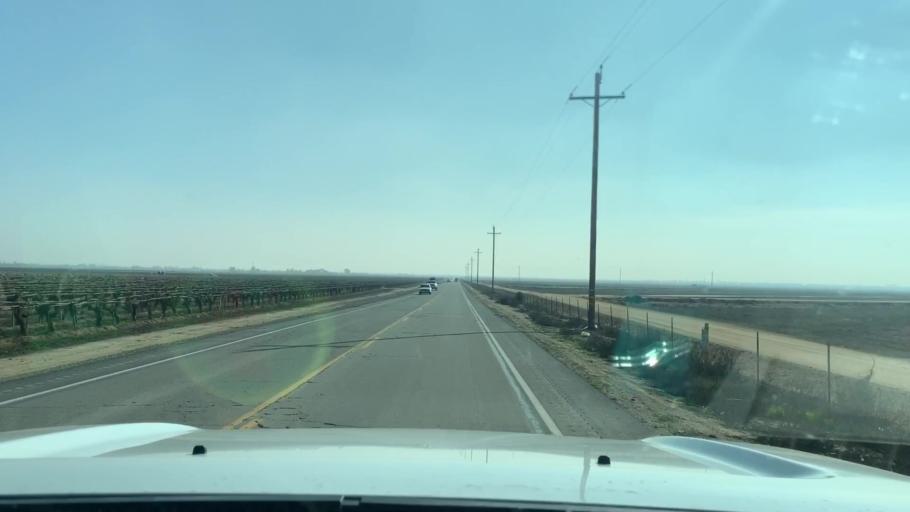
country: US
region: California
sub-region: Kern County
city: Rosedale
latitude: 35.4671
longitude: -119.1536
